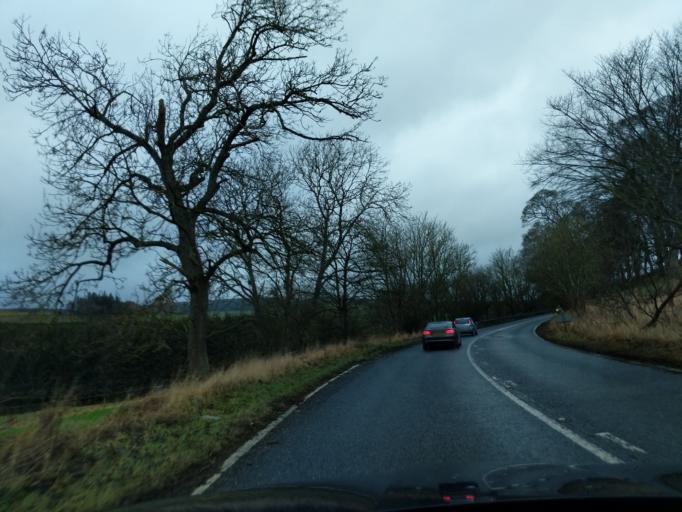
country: GB
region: Scotland
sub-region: The Scottish Borders
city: Galashiels
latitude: 55.6550
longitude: -2.8679
